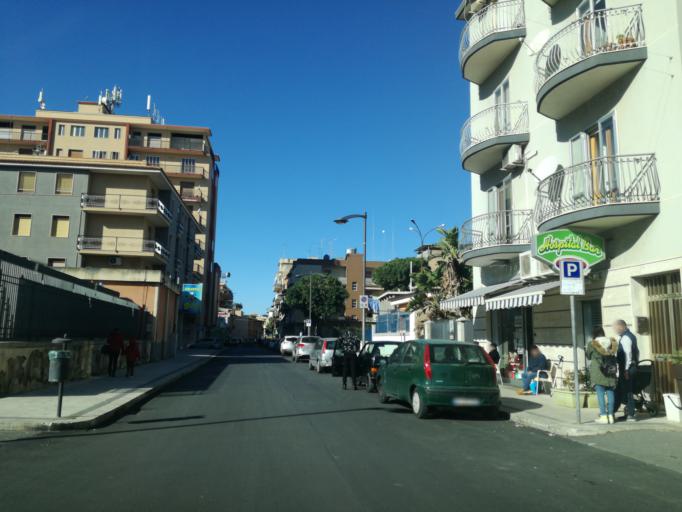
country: IT
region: Sicily
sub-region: Provincia di Caltanissetta
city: Gela
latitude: 37.0738
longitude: 14.2303
